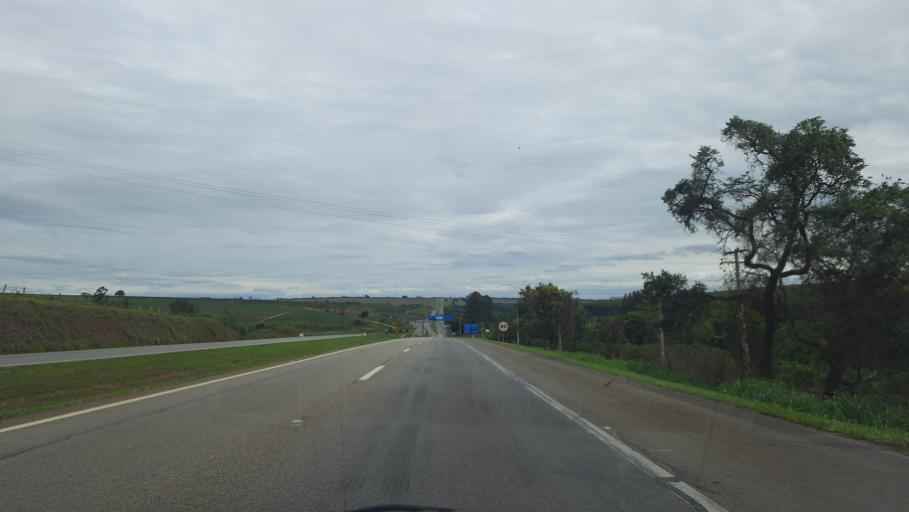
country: BR
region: Sao Paulo
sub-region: Aguai
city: Aguai
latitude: -22.1536
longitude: -46.9944
